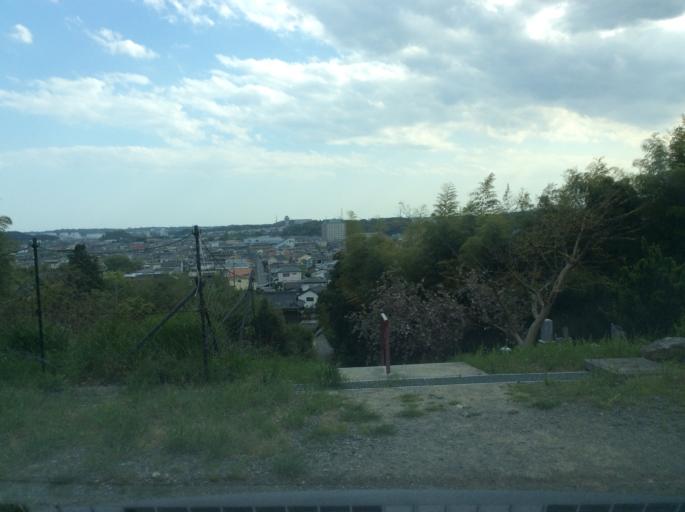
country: JP
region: Fukushima
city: Iwaki
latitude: 36.9618
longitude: 140.8567
